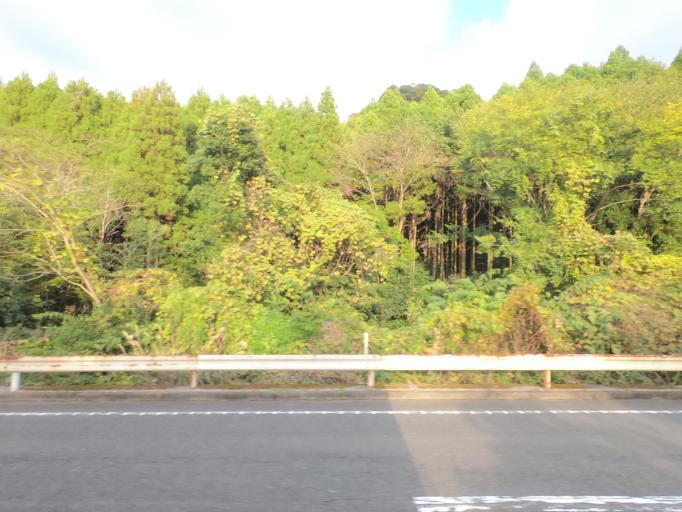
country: JP
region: Kumamoto
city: Minamata
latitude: 32.2427
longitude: 130.4802
